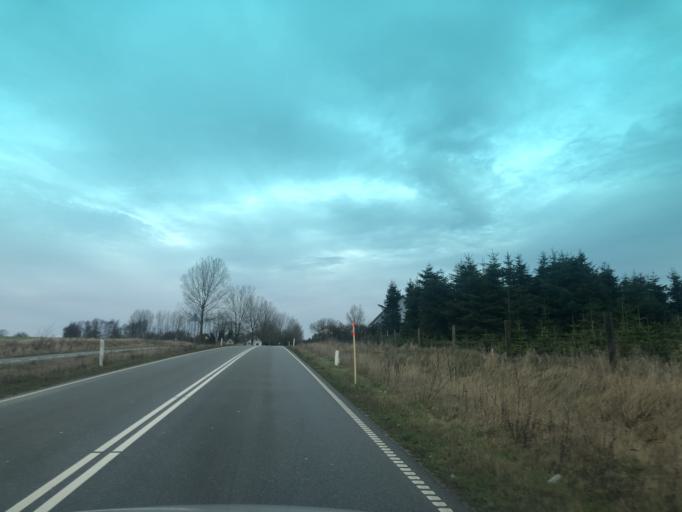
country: DK
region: Capital Region
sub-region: Frederikssund Kommune
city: Slangerup
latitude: 55.8765
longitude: 12.1929
